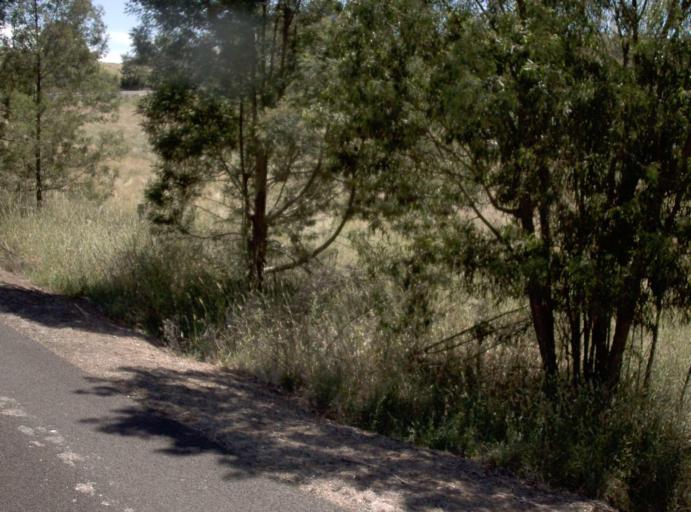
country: AU
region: Victoria
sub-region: East Gippsland
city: Lakes Entrance
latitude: -37.4049
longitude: 148.2113
